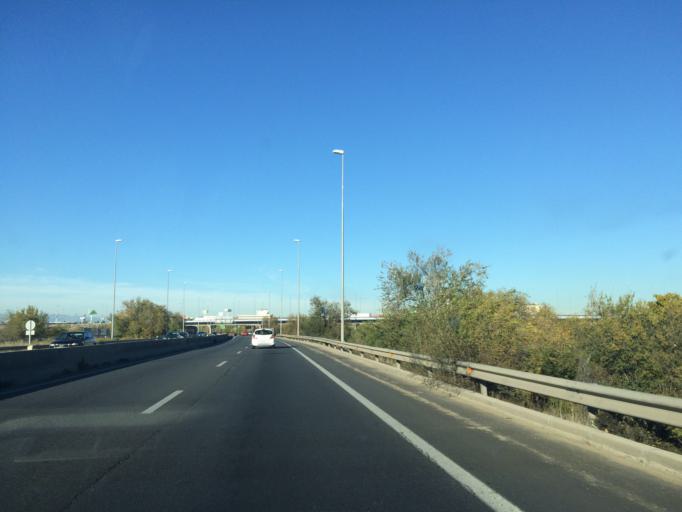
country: ES
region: Madrid
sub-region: Provincia de Madrid
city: Mostoles
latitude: 40.3347
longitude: -3.8520
